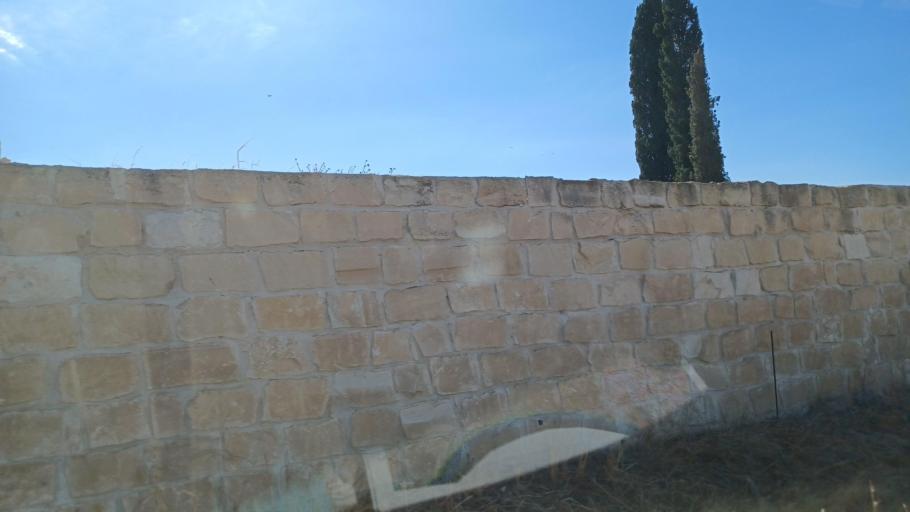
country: CY
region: Larnaka
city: Troulloi
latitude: 35.0105
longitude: 33.5861
